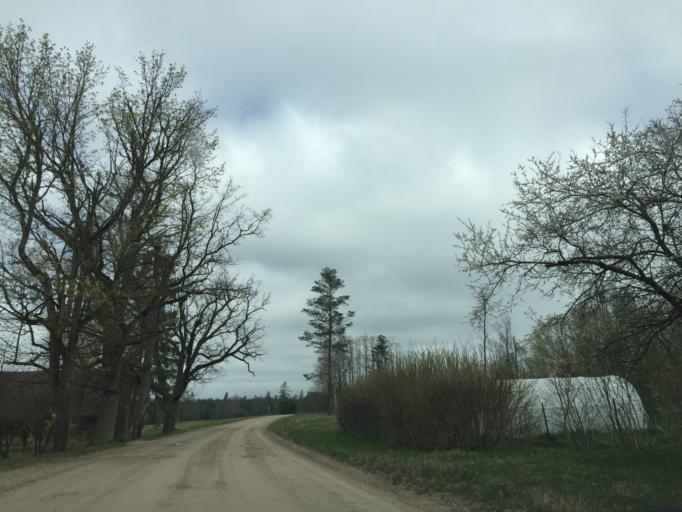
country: EE
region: Valgamaa
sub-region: Valga linn
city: Valga
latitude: 57.6040
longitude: 26.2275
